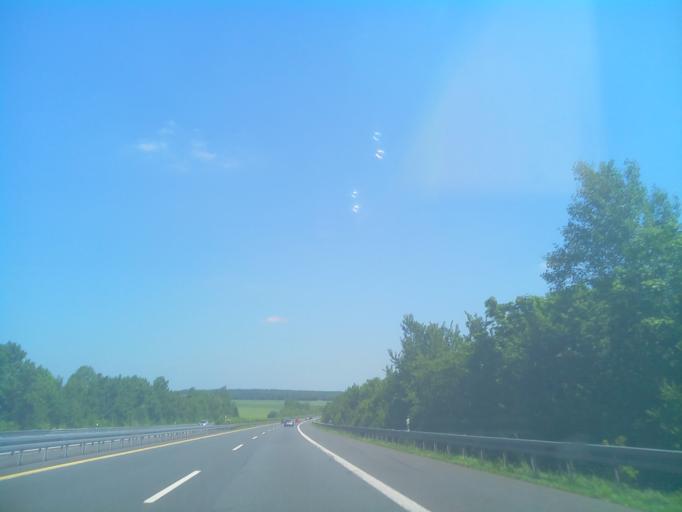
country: DE
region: Baden-Wuerttemberg
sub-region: Regierungsbezirk Stuttgart
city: Grossrinderfeld
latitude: 49.6476
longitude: 9.7367
